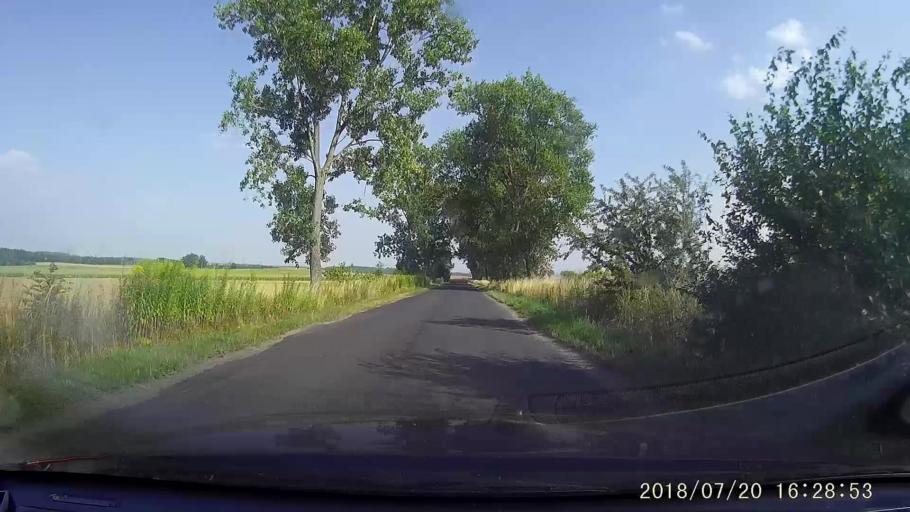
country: PL
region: Lower Silesian Voivodeship
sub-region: Powiat zgorzelecki
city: Sulikow
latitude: 51.1164
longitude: 15.0614
